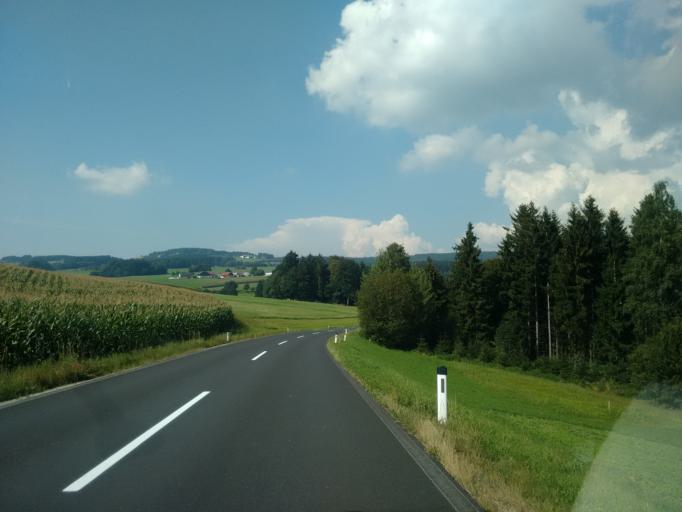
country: AT
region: Upper Austria
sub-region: Politischer Bezirk Urfahr-Umgebung
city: Altenberg bei Linz
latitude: 48.3975
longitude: 14.3451
